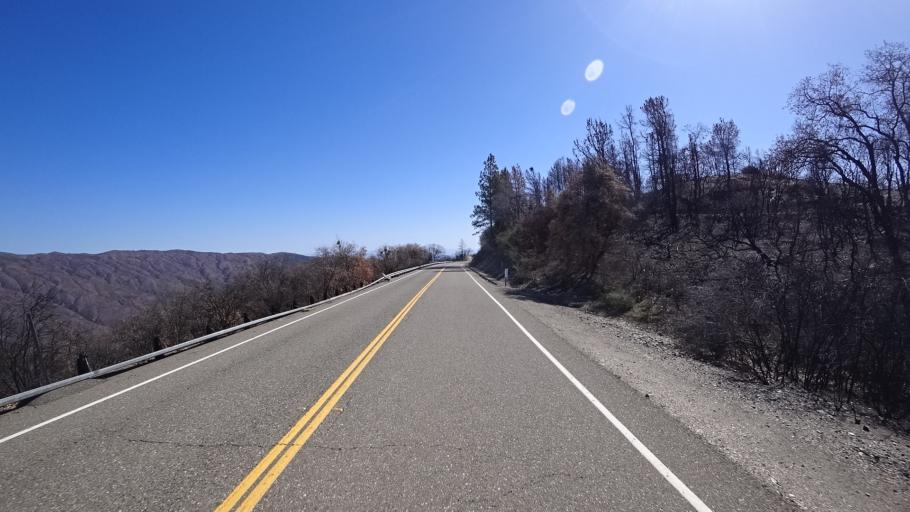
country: US
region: California
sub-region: Tehama County
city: Rancho Tehama Reserve
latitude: 39.6675
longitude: -122.6775
